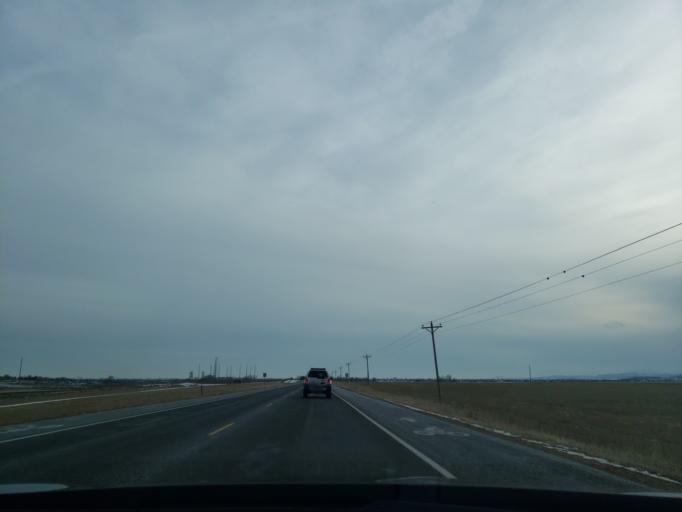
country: US
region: Colorado
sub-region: Larimer County
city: Loveland
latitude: 40.4658
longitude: -105.0965
